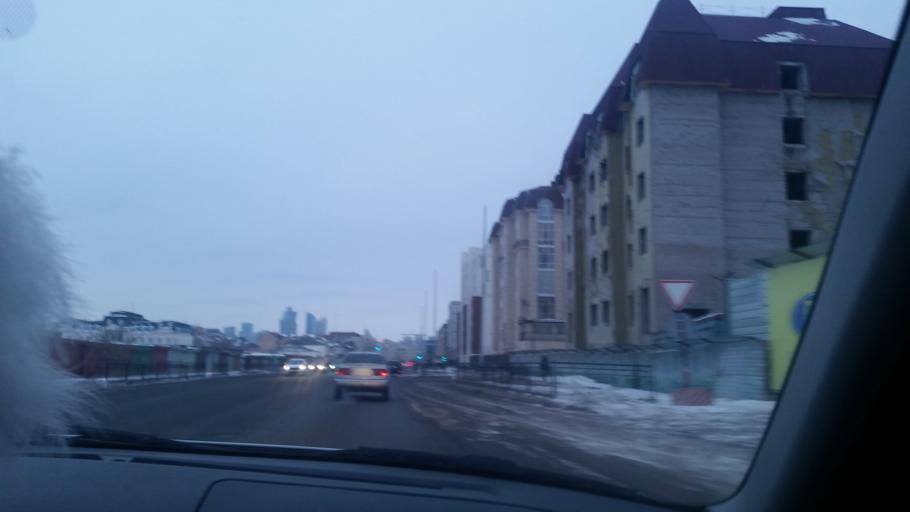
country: KZ
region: Astana Qalasy
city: Astana
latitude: 51.1440
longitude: 71.4573
